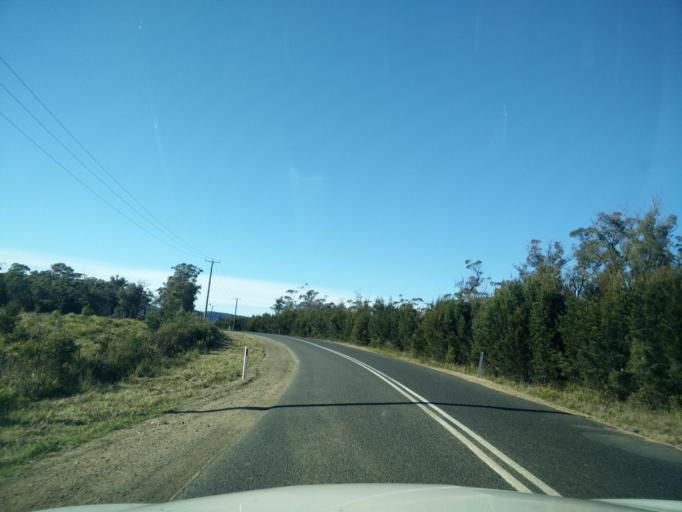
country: AU
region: Tasmania
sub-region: Break O'Day
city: St Helens
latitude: -41.8973
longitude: 148.2550
